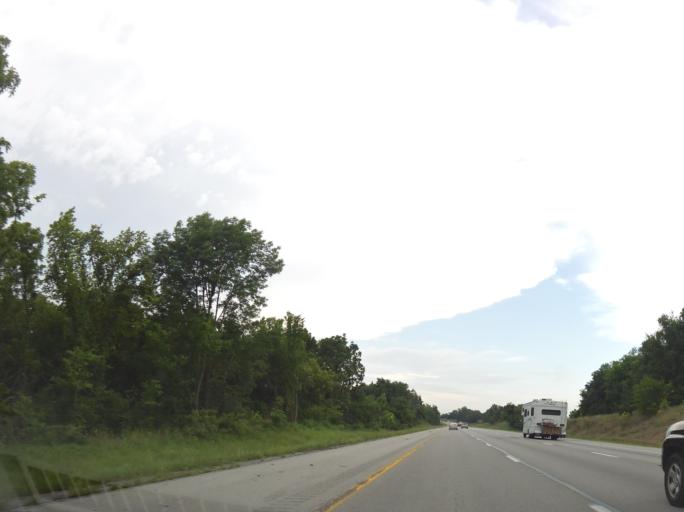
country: US
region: Kentucky
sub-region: Madison County
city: Berea
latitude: 37.6567
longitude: -84.3110
